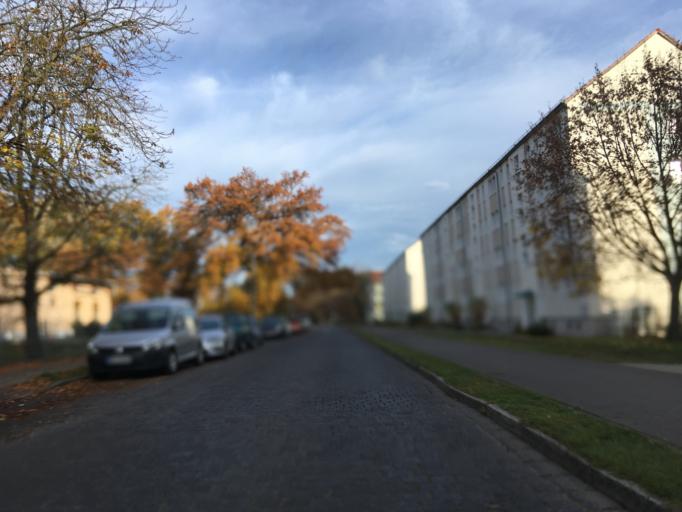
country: DE
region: Brandenburg
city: Luebben
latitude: 51.9485
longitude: 13.8850
